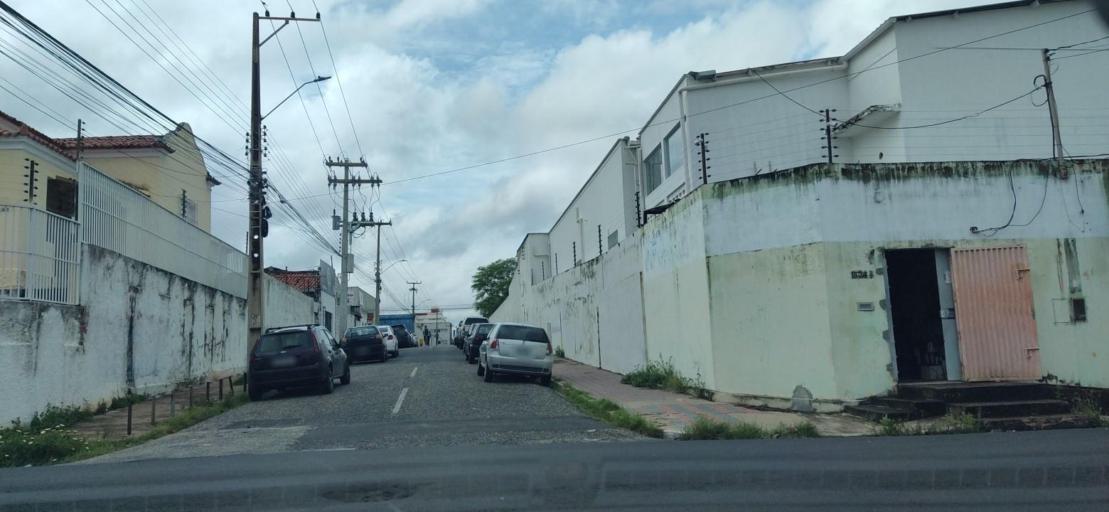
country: BR
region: Piaui
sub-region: Teresina
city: Teresina
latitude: -5.0861
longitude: -42.8102
